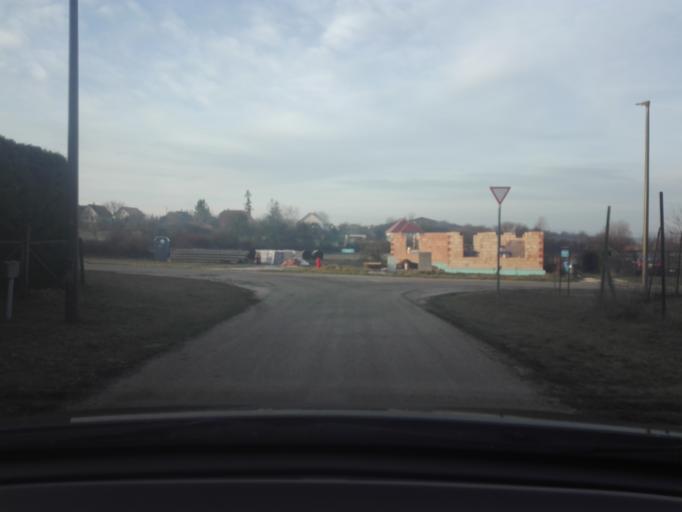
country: HU
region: Veszprem
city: Balatonfured
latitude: 47.0099
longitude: 17.7803
